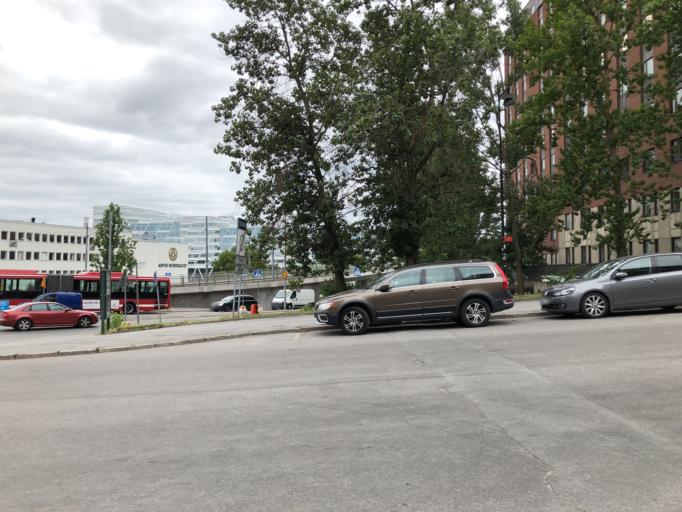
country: SE
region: Stockholm
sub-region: Sundbybergs Kommun
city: Sundbyberg
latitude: 59.3616
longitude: 17.9769
